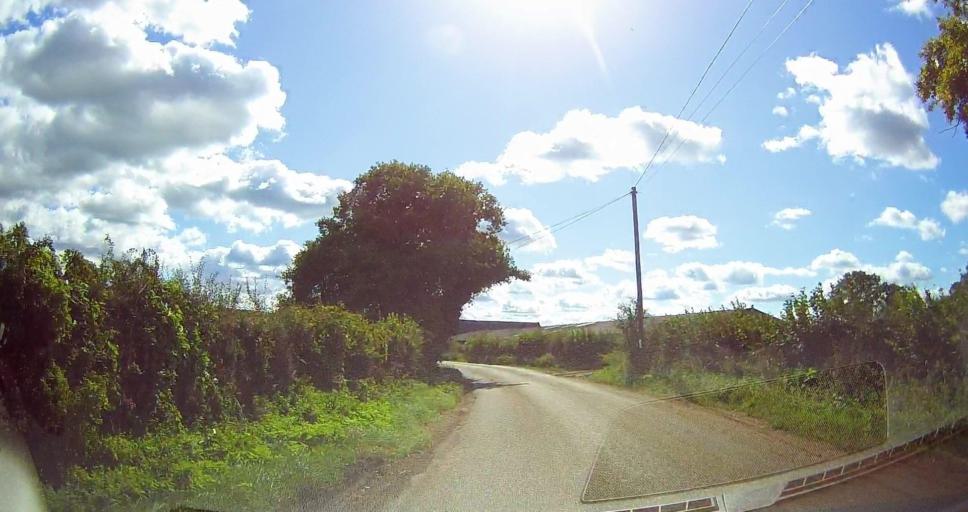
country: GB
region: England
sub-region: Cheshire East
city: Nantwich
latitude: 52.9908
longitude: -2.5344
